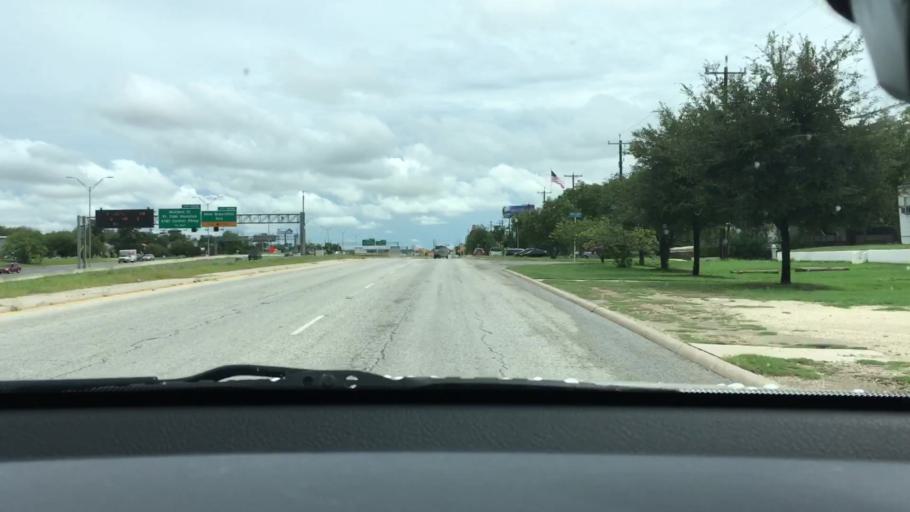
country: US
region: Texas
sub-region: Bexar County
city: San Antonio
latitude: 29.4379
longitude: -98.4692
